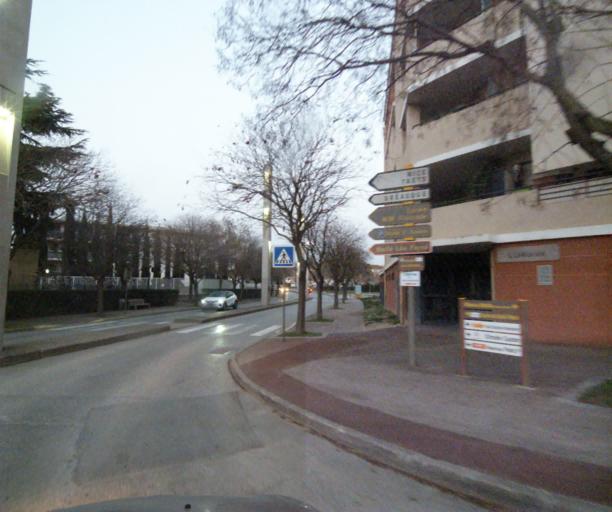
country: FR
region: Provence-Alpes-Cote d'Azur
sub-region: Departement des Bouches-du-Rhone
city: Gardanne
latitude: 43.4514
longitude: 5.4728
